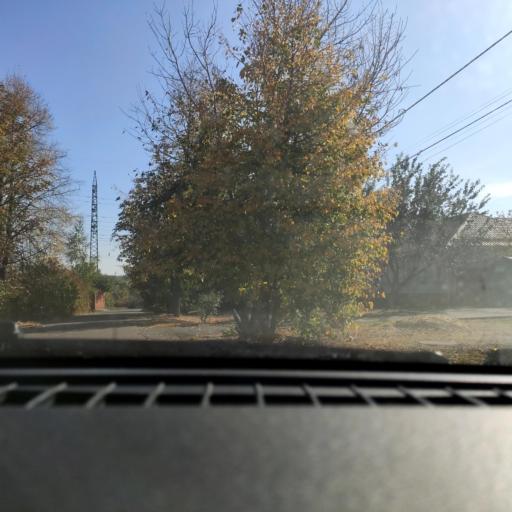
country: RU
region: Voronezj
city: Maslovka
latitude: 51.6150
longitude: 39.2711
